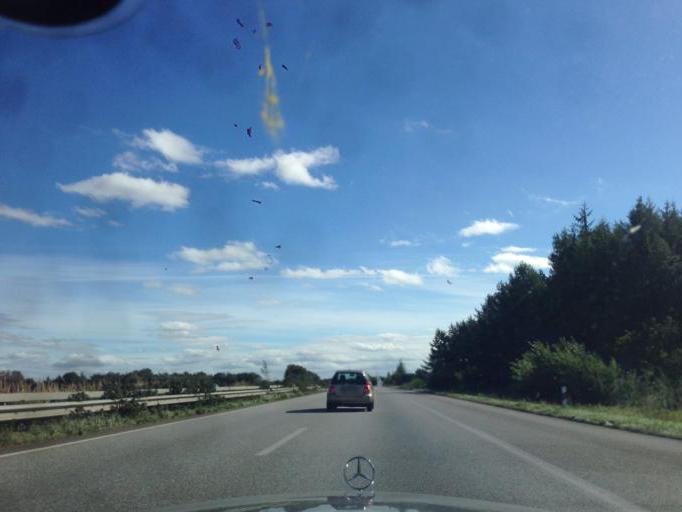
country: DE
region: Schleswig-Holstein
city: Bollingstedt
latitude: 54.6112
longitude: 9.4454
